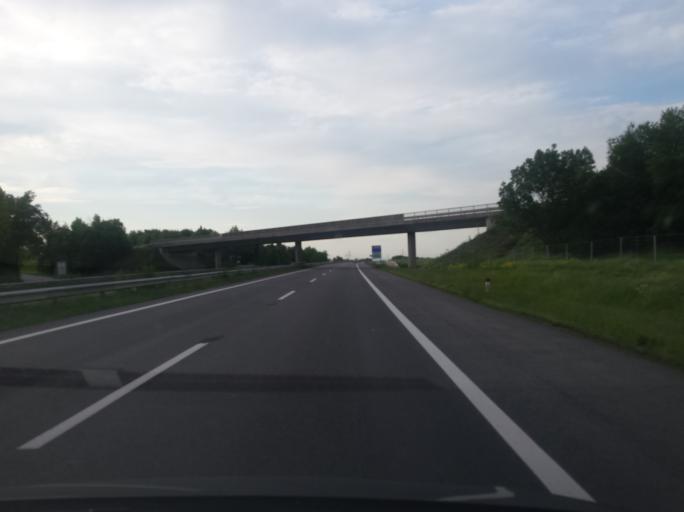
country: AT
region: Burgenland
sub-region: Eisenstadt-Umgebung
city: Steinbrunn
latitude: 47.8563
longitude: 16.4243
